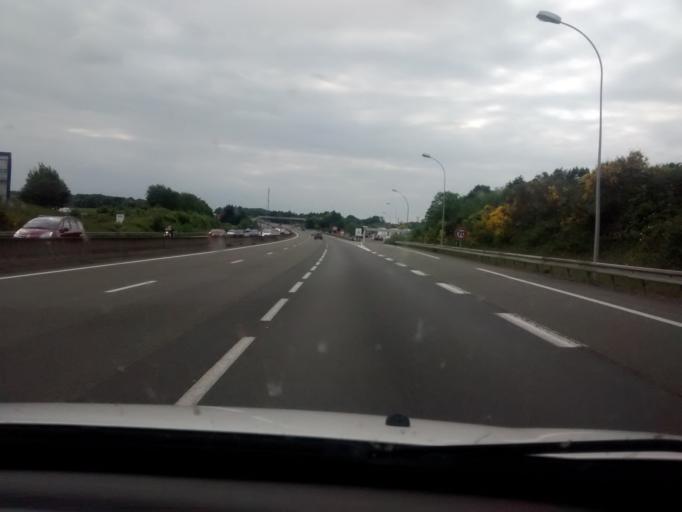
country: FR
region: Pays de la Loire
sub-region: Departement de la Sarthe
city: Sarge-les-le-Mans
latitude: 48.0541
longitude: 0.2592
